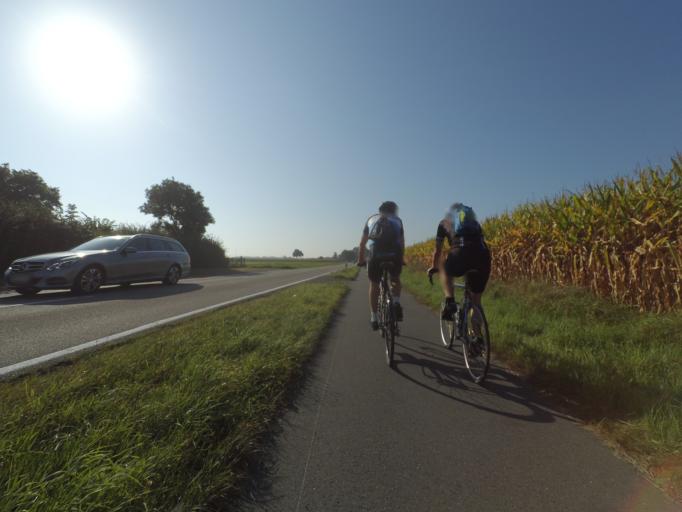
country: DE
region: Lower Saxony
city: Ohne
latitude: 52.2391
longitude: 7.2956
